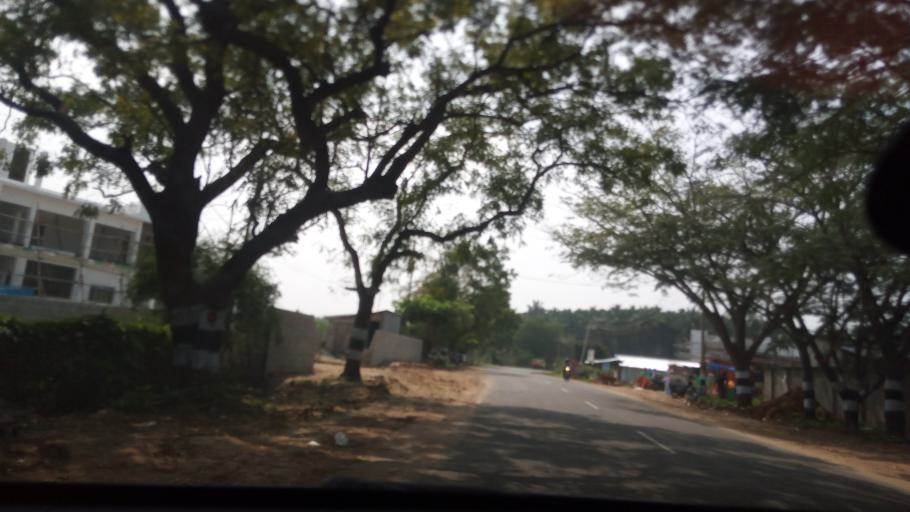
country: IN
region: Tamil Nadu
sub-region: Coimbatore
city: Perur
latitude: 11.0169
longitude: 76.8787
